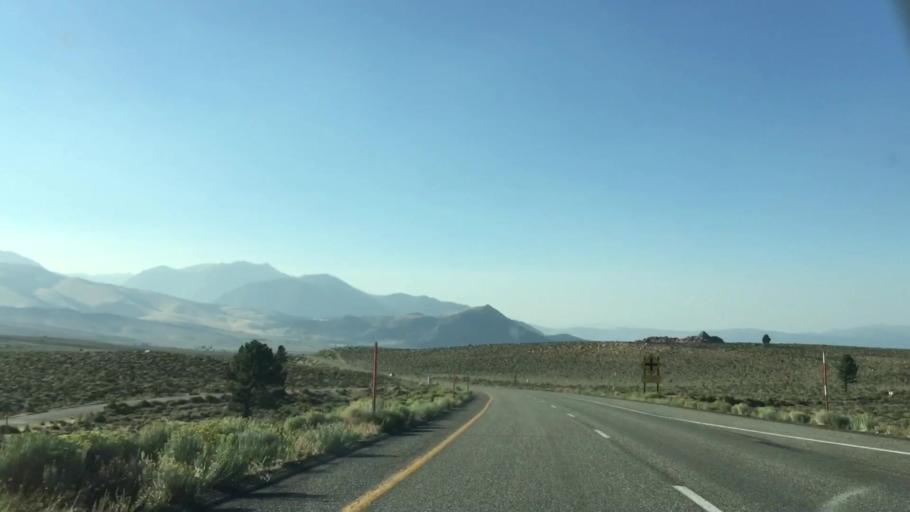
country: US
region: California
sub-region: Mono County
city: Mammoth Lakes
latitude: 37.8405
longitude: -119.0710
